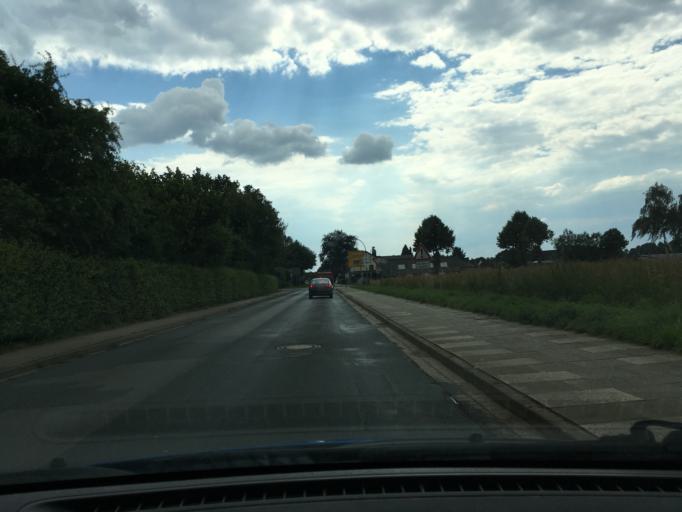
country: DE
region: Lower Saxony
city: Bendestorf
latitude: 53.3668
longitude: 9.9342
